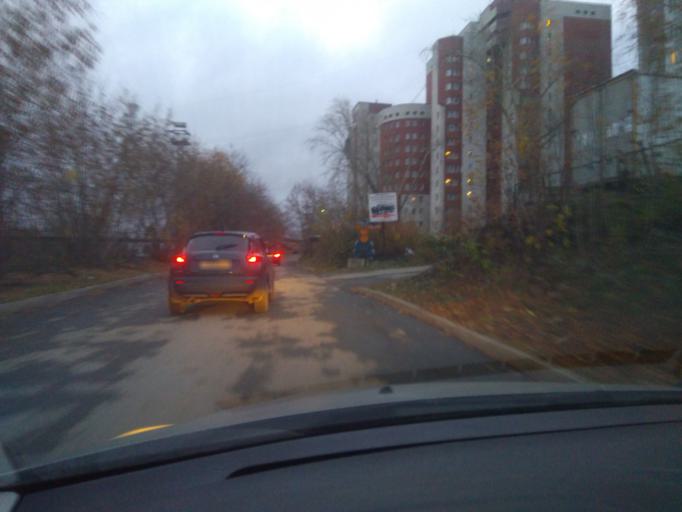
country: RU
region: Sverdlovsk
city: Yekaterinburg
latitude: 56.8548
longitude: 60.5843
